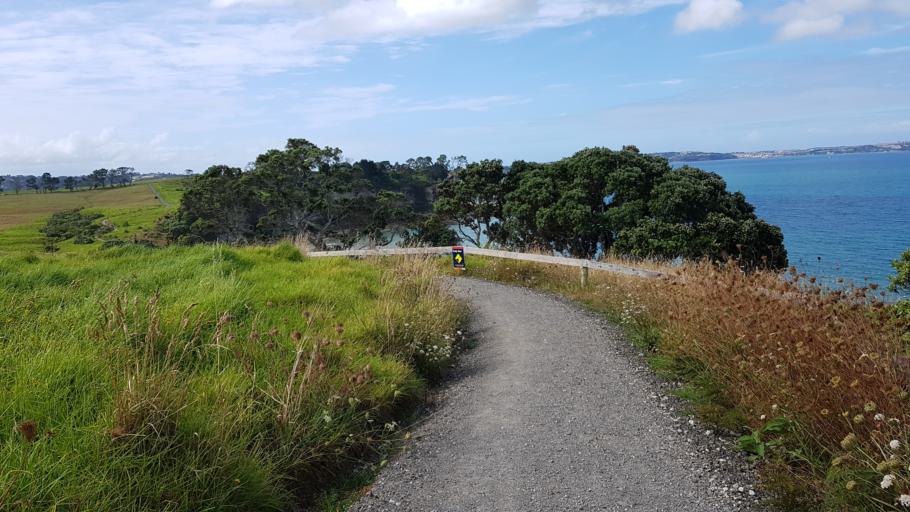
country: NZ
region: Auckland
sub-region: Auckland
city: Rothesay Bay
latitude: -36.6711
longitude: 174.7471
